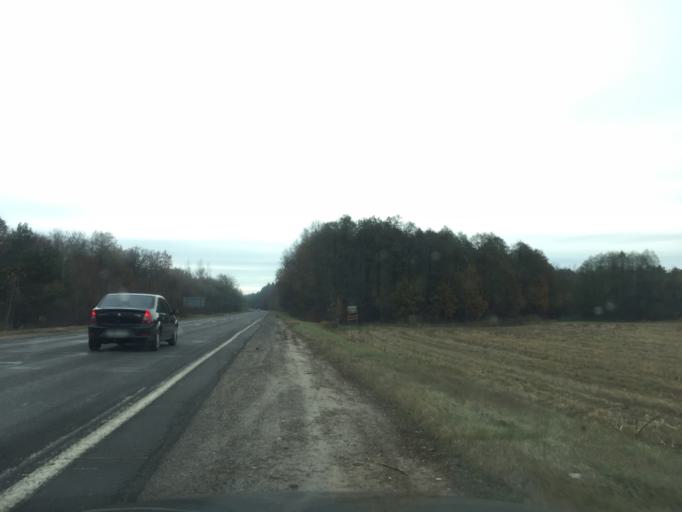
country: BY
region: Gomel
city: Gomel
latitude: 52.3965
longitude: 30.8288
